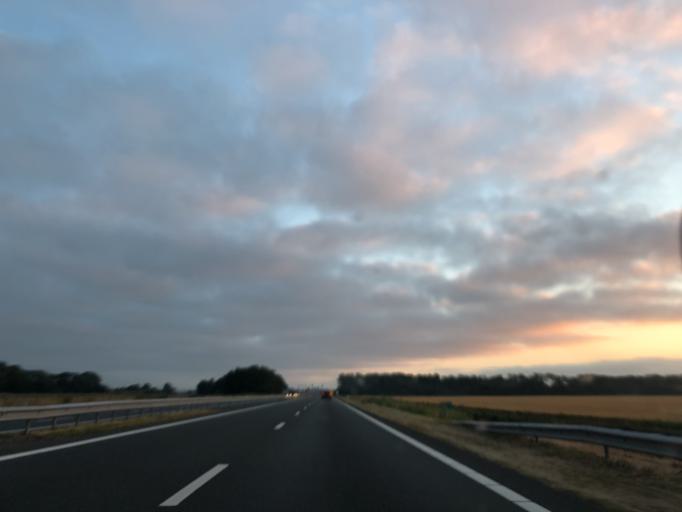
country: NL
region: Groningen
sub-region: Gemeente Veendam
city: Veendam
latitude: 53.1552
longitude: 6.8963
